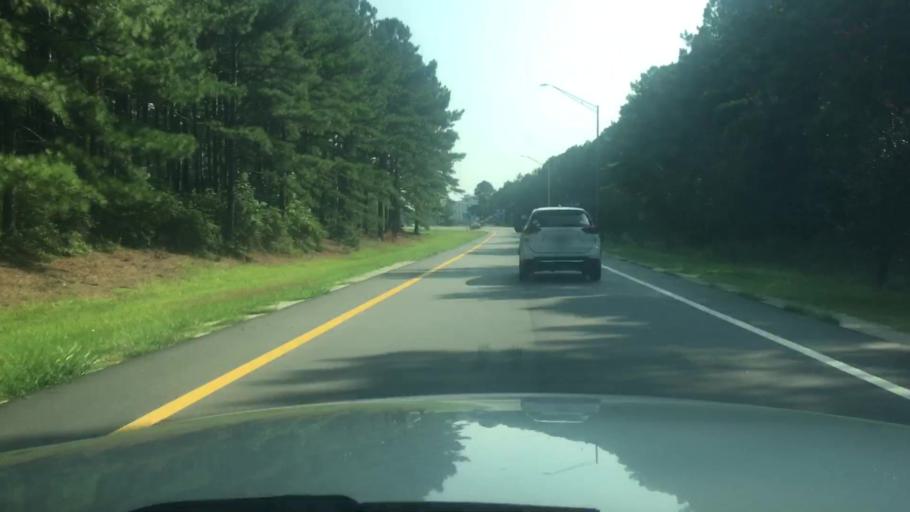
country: US
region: North Carolina
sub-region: Cumberland County
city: Vander
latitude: 35.0048
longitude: -78.8209
